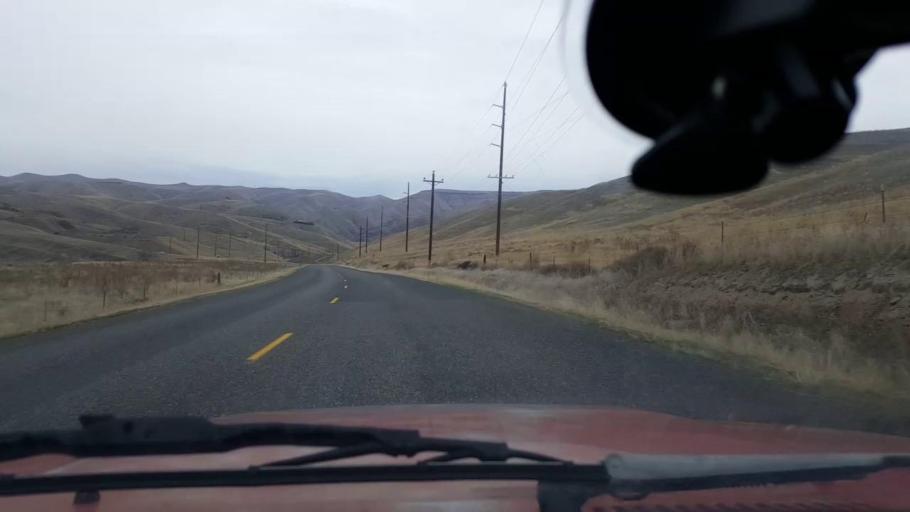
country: US
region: Washington
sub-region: Asotin County
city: Clarkston Heights-Vineland
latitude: 46.4051
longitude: -117.1035
